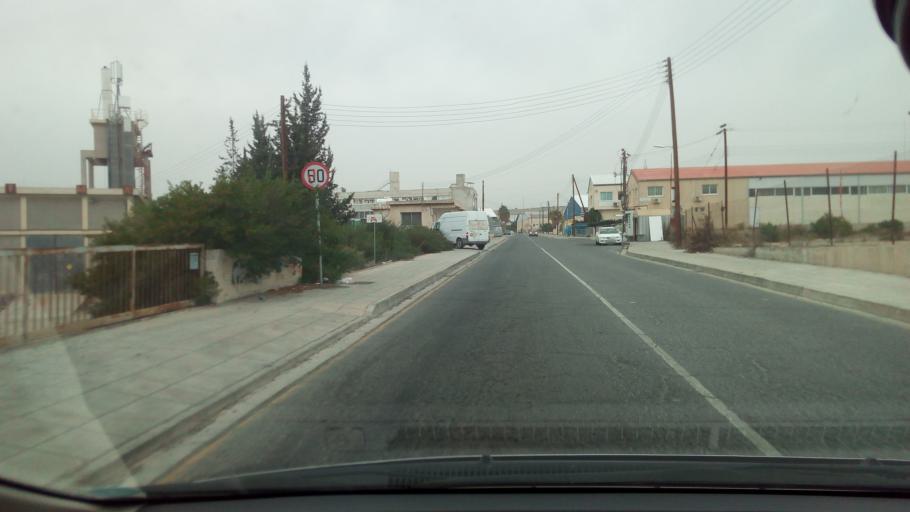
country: CY
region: Limassol
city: Ypsonas
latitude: 34.7017
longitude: 32.9558
